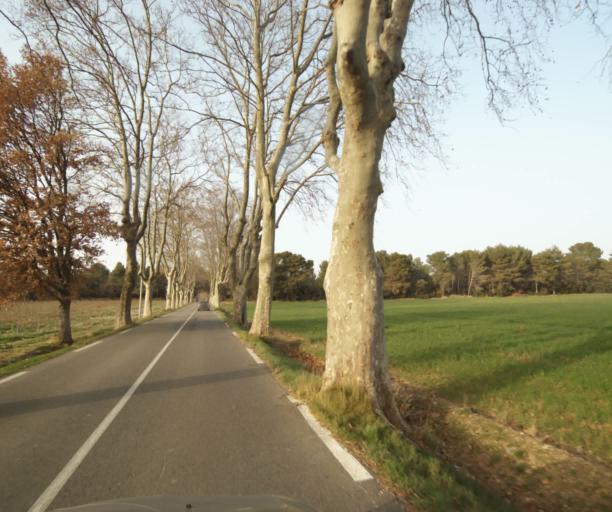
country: FR
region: Provence-Alpes-Cote d'Azur
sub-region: Departement des Bouches-du-Rhone
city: Eguilles
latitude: 43.6052
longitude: 5.3658
